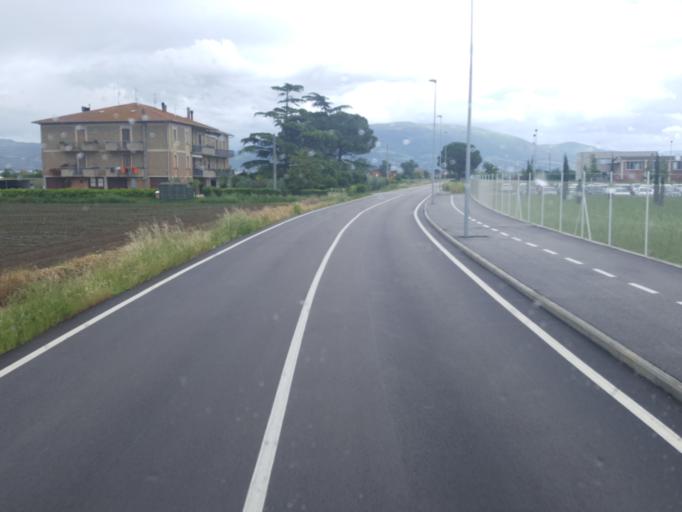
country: IT
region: Umbria
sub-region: Provincia di Perugia
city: Ospedalicchio
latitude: 43.0710
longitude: 12.5053
